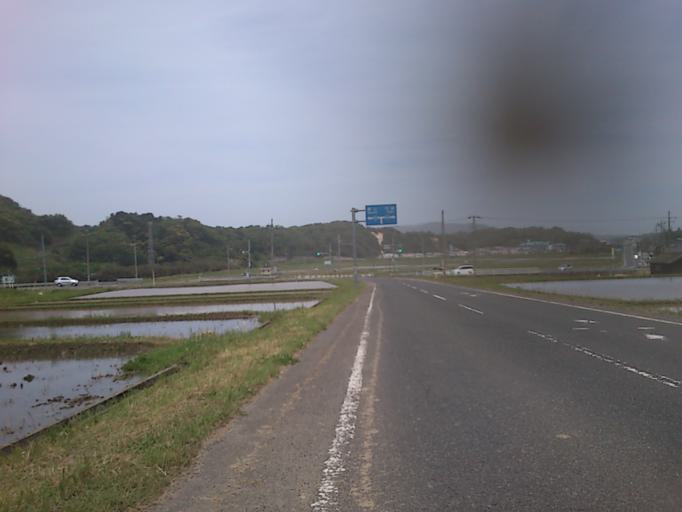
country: JP
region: Kyoto
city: Miyazu
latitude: 35.6415
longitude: 135.0879
